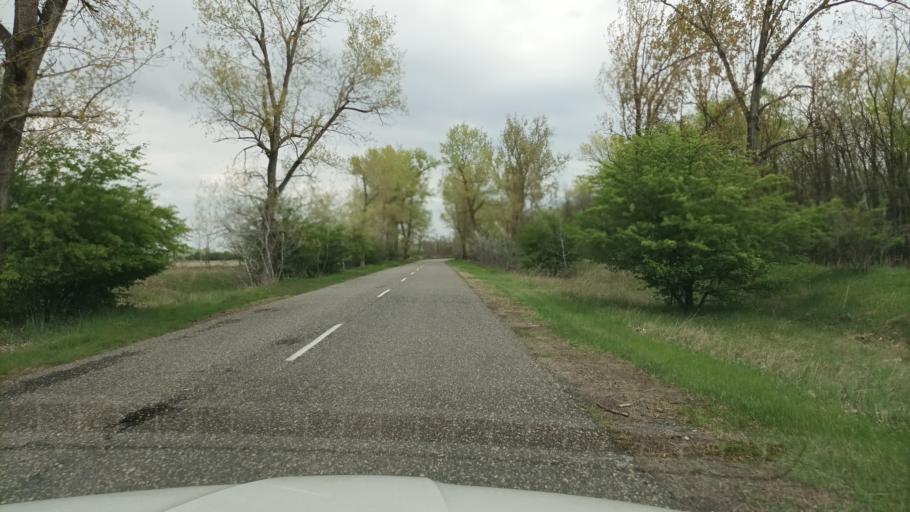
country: HU
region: Pest
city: Tortel
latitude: 47.0832
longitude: 19.8742
